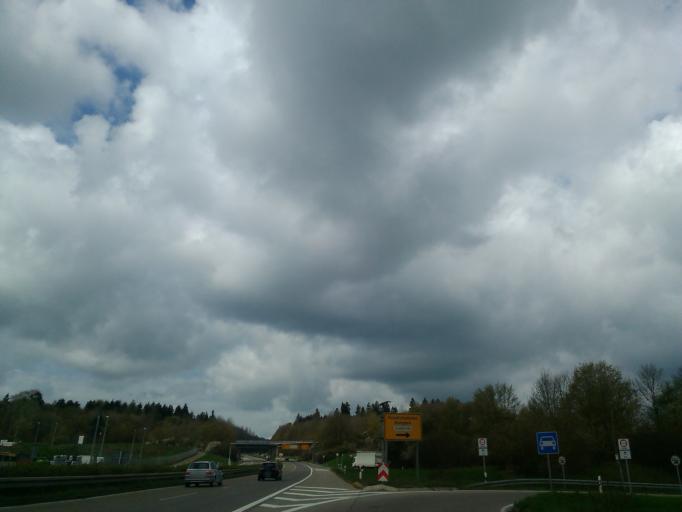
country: DE
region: Baden-Wuerttemberg
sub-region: Tuebingen Region
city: Ulm
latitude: 48.4262
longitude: 9.9736
